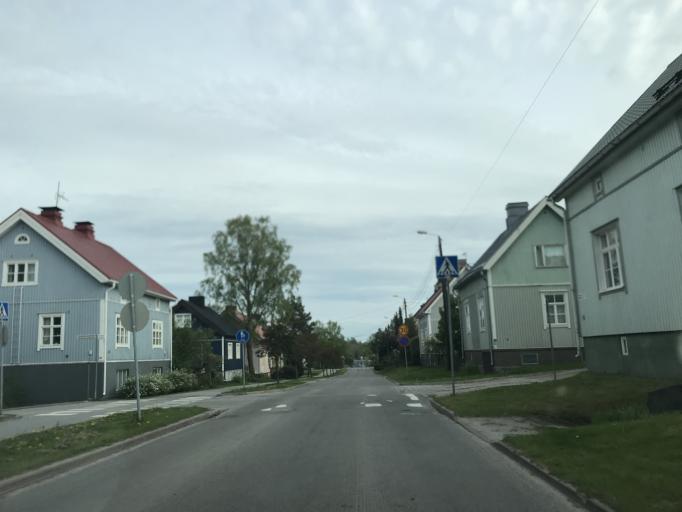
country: FI
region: Varsinais-Suomi
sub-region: Turku
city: Turku
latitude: 60.4530
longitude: 22.3081
